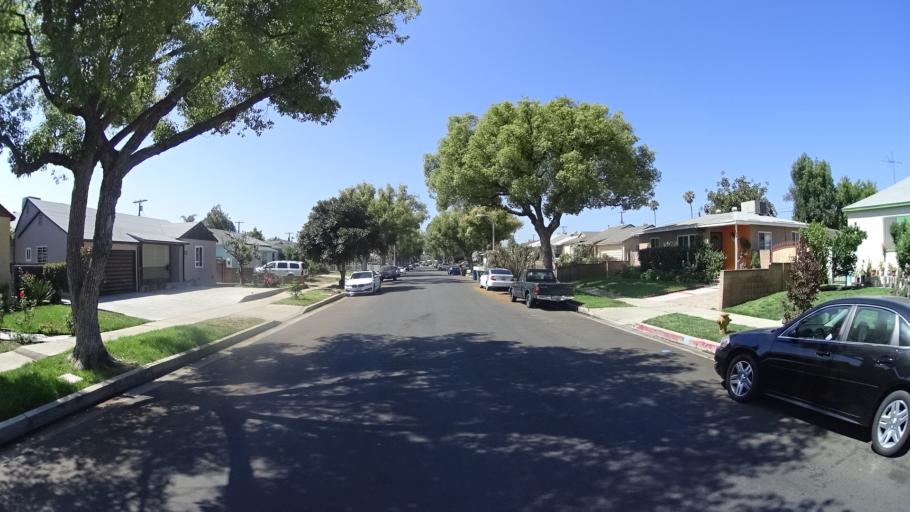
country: US
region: California
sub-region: Los Angeles County
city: Van Nuys
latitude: 34.2313
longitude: -118.4412
